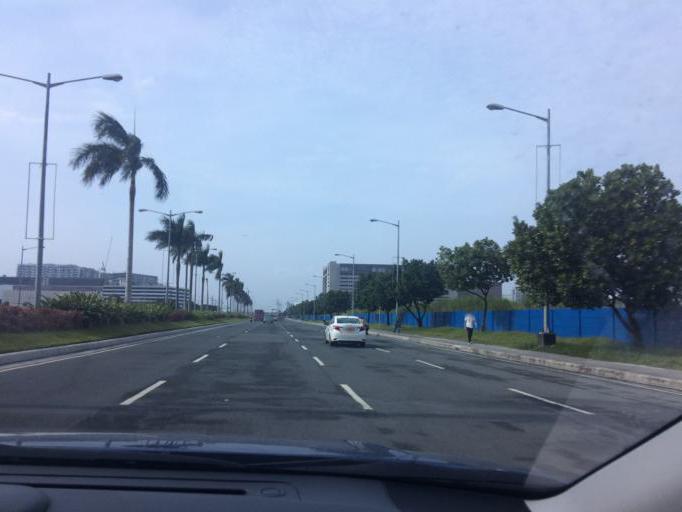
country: PH
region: Metro Manila
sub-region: Makati City
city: Makati City
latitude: 14.5283
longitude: 120.9848
